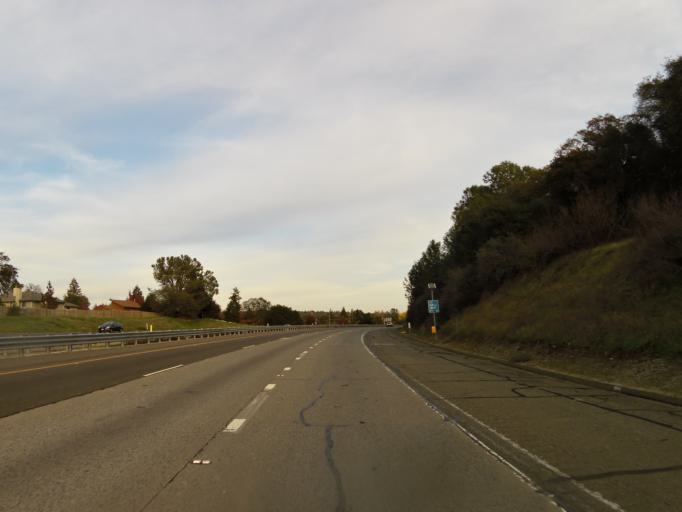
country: US
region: California
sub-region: El Dorado County
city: Cameron Park
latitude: 38.6588
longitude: -120.9806
